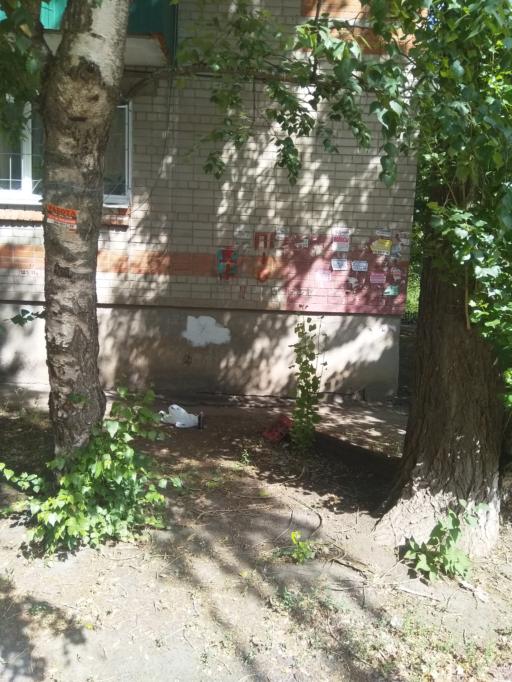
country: RU
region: Voronezj
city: Voronezh
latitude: 51.6494
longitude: 39.1546
